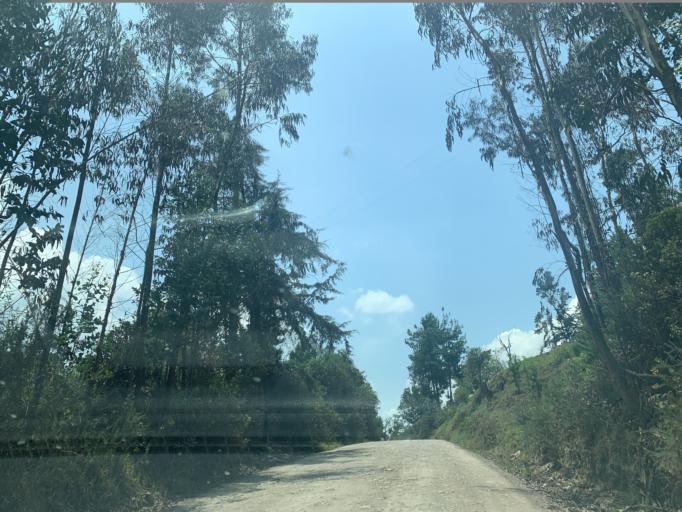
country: CO
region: Boyaca
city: Chiquinquira
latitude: 5.5897
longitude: -73.7536
